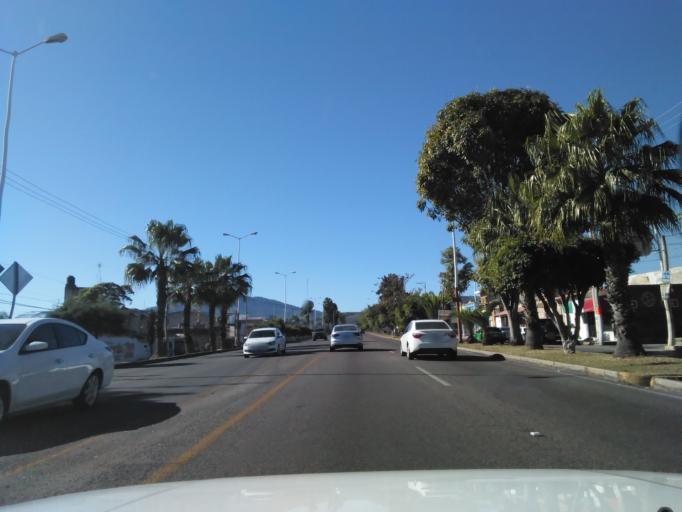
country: MX
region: Nayarit
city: Xalisco
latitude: 21.4582
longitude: -104.8942
